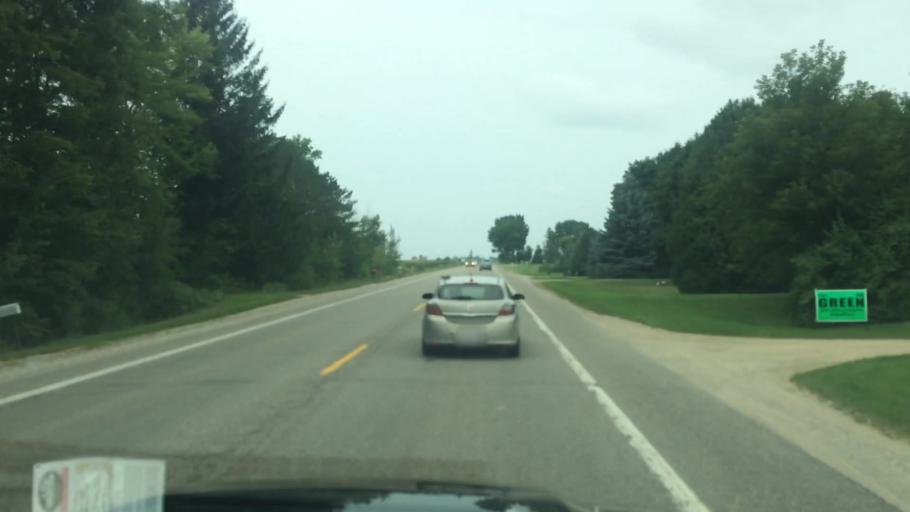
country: US
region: Michigan
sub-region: Huron County
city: Bad Axe
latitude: 43.9014
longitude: -83.0036
